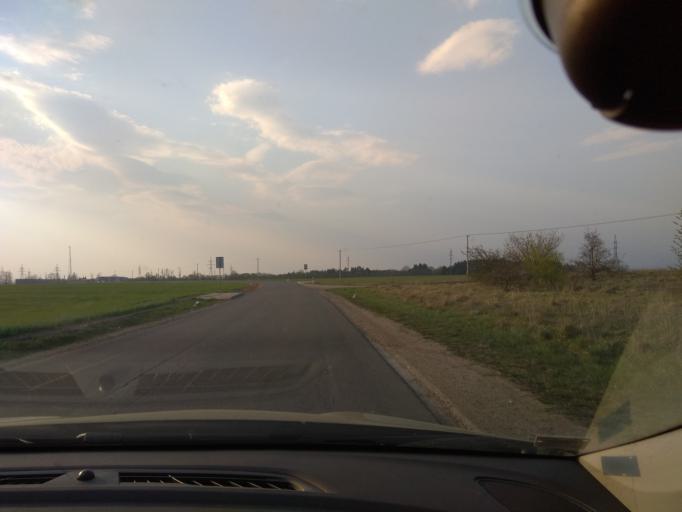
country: LT
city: Baltoji Voke
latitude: 54.6079
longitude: 25.1297
